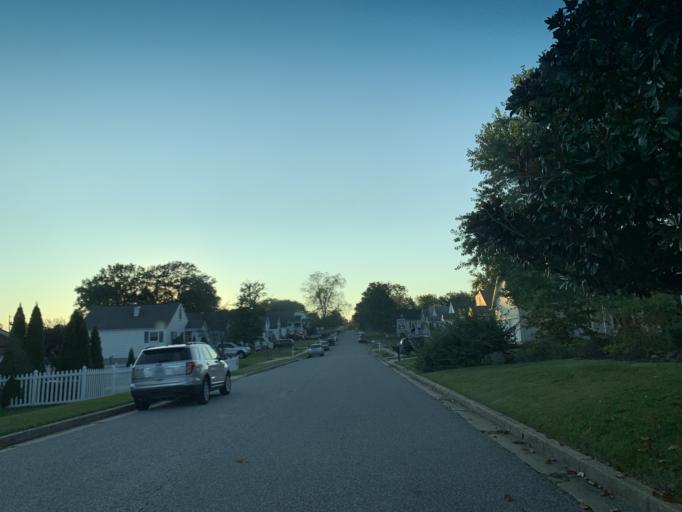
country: US
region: Maryland
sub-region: Baltimore County
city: Perry Hall
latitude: 39.4029
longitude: -76.4711
